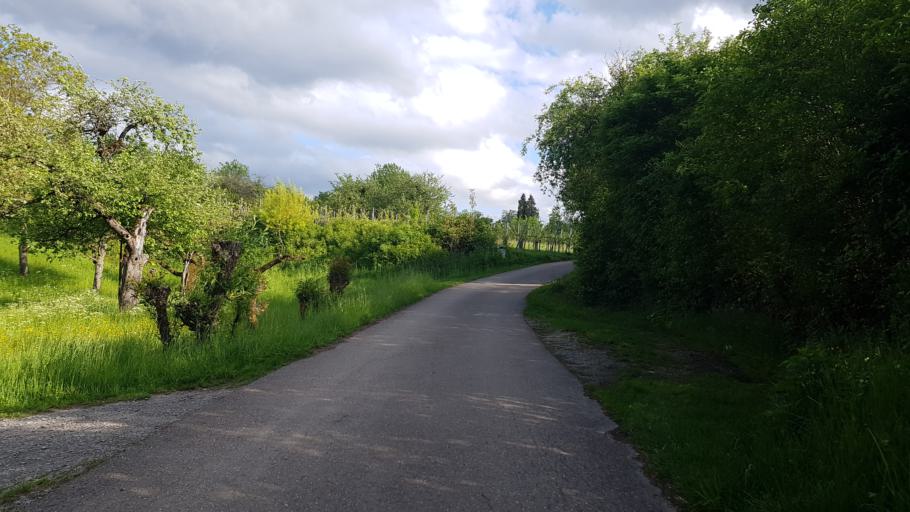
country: DE
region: Baden-Wuerttemberg
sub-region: Regierungsbezirk Stuttgart
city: Marbach am Neckar
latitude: 48.9507
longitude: 9.2555
